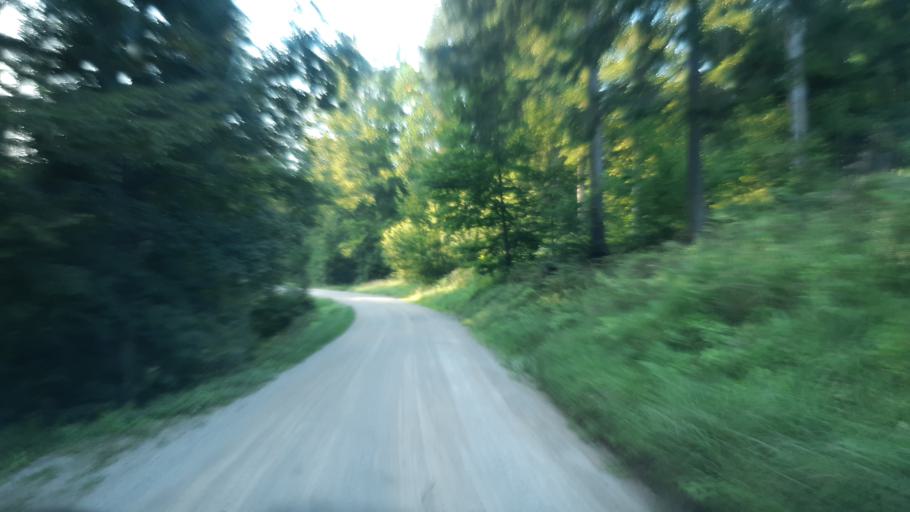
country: SI
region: Kocevje
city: Kocevje
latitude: 45.6664
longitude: 14.9613
